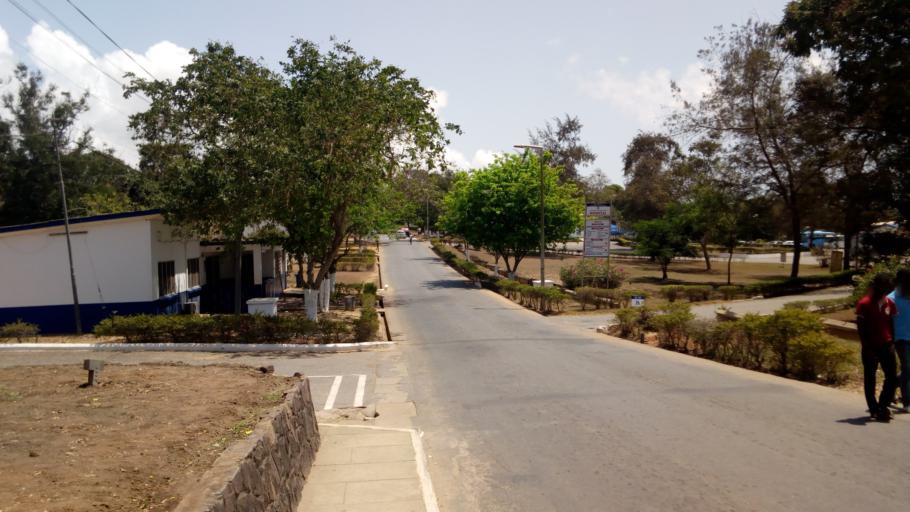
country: GH
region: Central
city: Cape Coast
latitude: 5.1054
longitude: -1.2838
